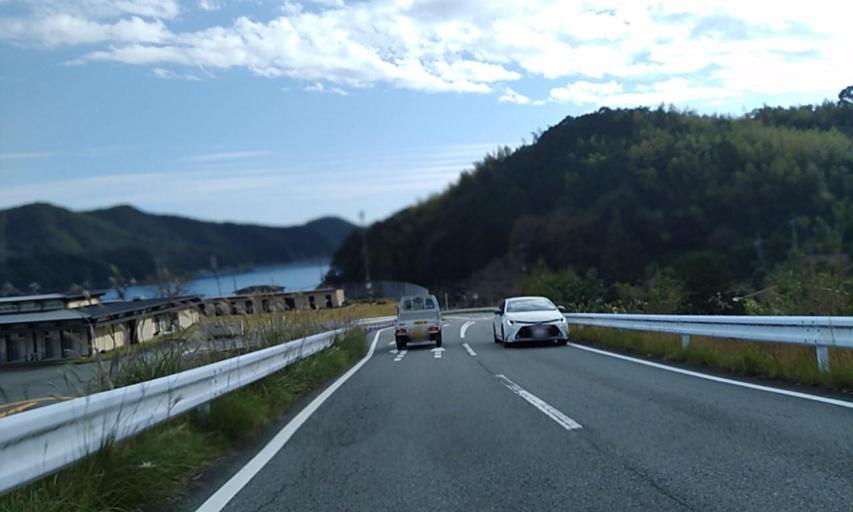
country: JP
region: Mie
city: Ise
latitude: 34.2902
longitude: 136.5686
